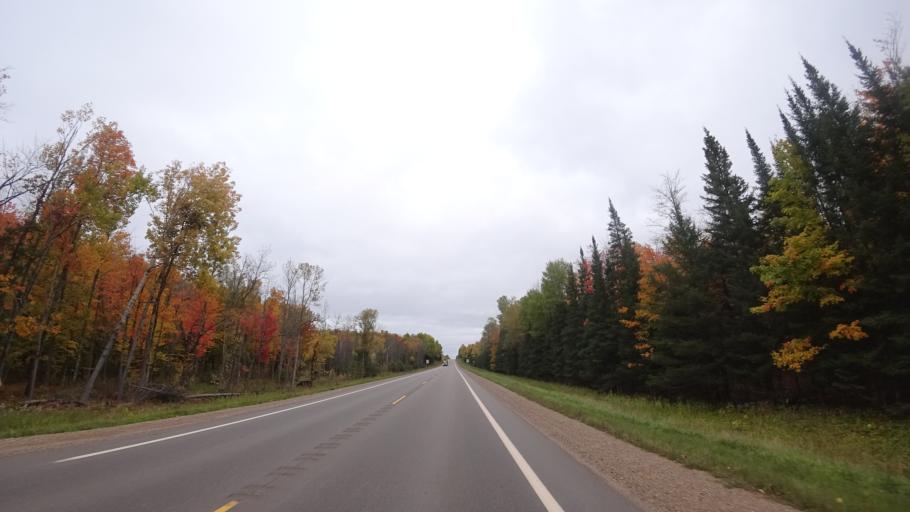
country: US
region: Michigan
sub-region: Iron County
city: Crystal Falls
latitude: 46.1775
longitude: -88.0490
